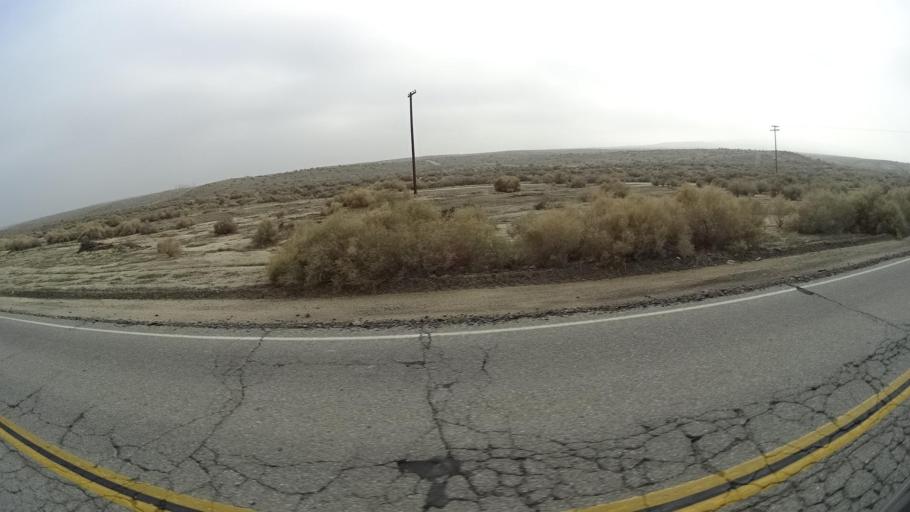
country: US
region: California
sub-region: Kern County
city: South Taft
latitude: 35.1360
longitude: -119.4092
